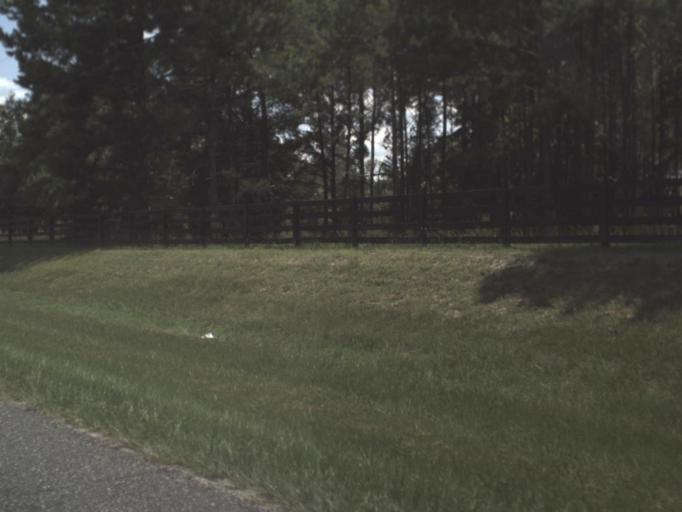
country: US
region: Florida
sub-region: Alachua County
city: High Springs
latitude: 29.8661
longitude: -82.6087
